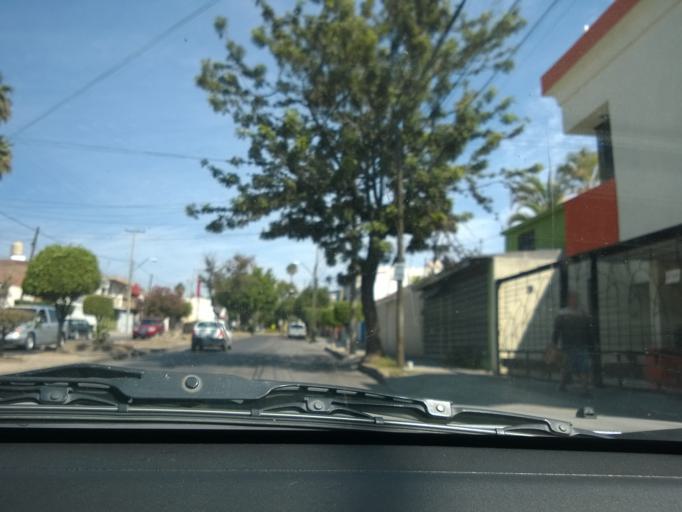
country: MX
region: Guanajuato
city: Leon
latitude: 21.1173
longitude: -101.6957
